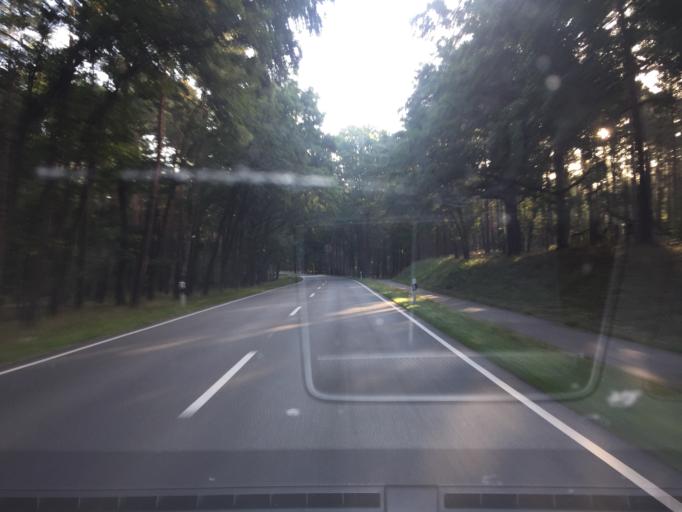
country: DE
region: Lower Saxony
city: Frankenfeld
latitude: 52.8034
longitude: 9.4292
